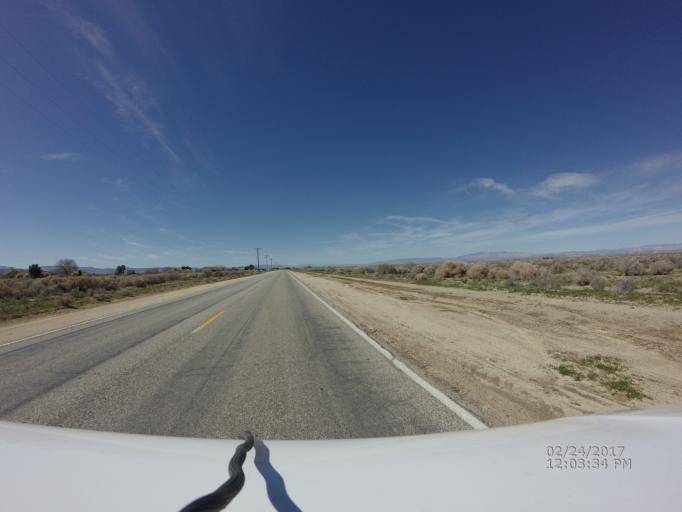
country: US
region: California
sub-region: Los Angeles County
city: Lancaster
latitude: 34.7191
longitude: -118.0439
